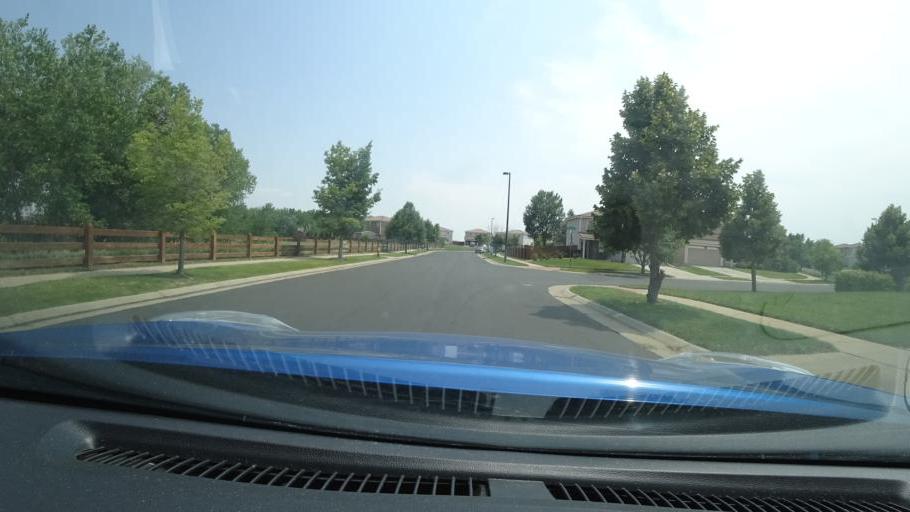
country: US
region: Colorado
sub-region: Adams County
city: Aurora
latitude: 39.7740
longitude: -104.7373
